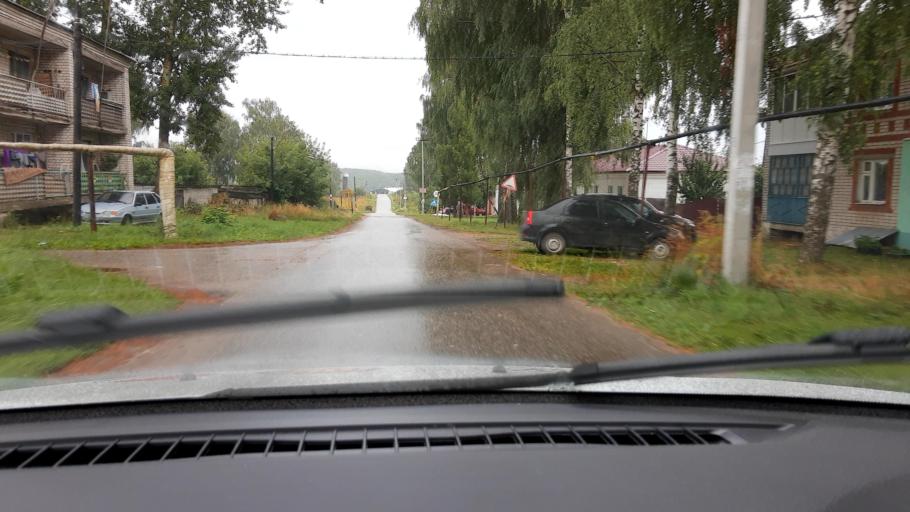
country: RU
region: Nizjnij Novgorod
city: Reshetikha
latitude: 56.1394
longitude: 43.3493
